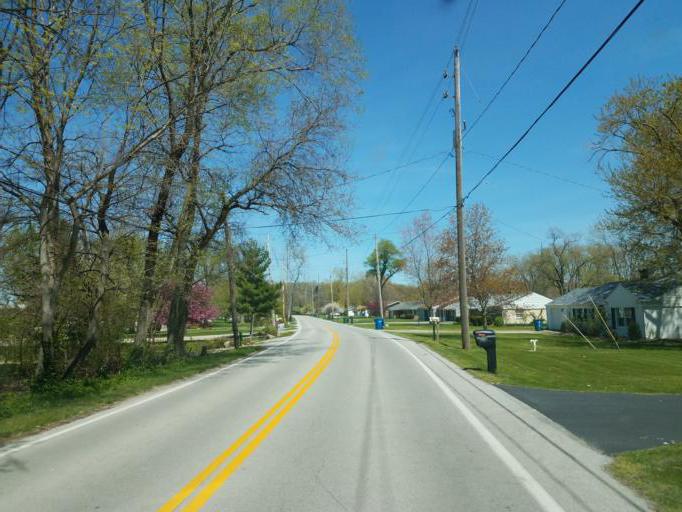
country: US
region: Ohio
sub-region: Ottawa County
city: Port Clinton
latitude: 41.5309
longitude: -82.8709
